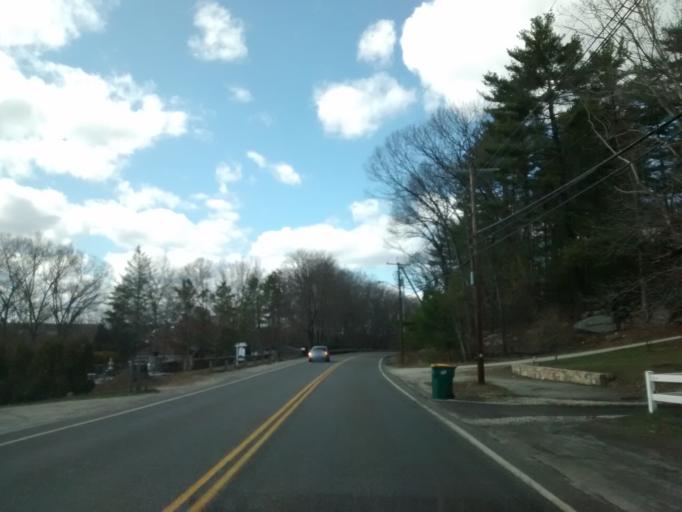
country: US
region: Massachusetts
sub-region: Worcester County
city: Northbridge
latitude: 42.1324
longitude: -71.6365
